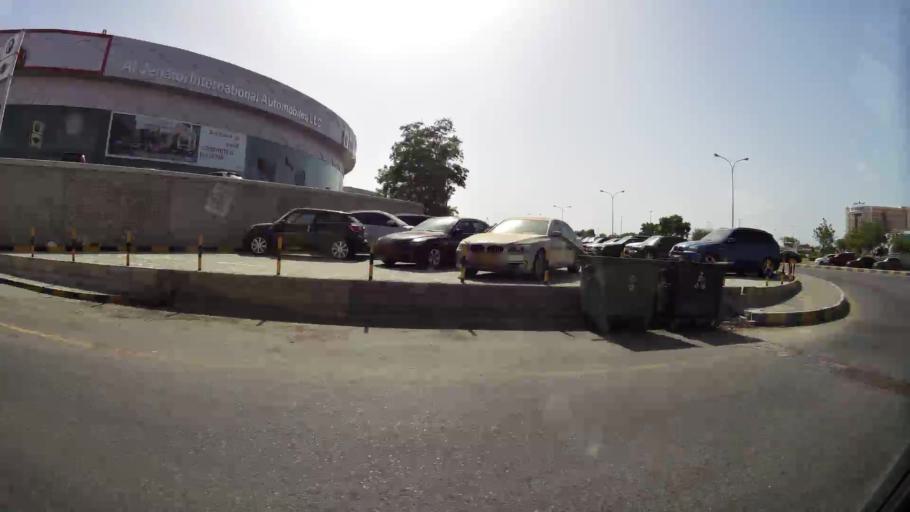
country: OM
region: Muhafazat Masqat
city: Muscat
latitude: 23.6094
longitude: 58.4952
